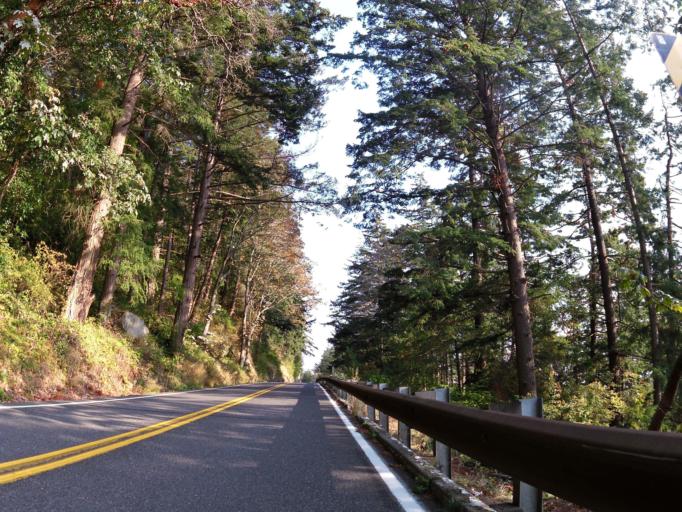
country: US
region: Washington
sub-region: Whatcom County
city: Bellingham
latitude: 48.6314
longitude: -122.4705
